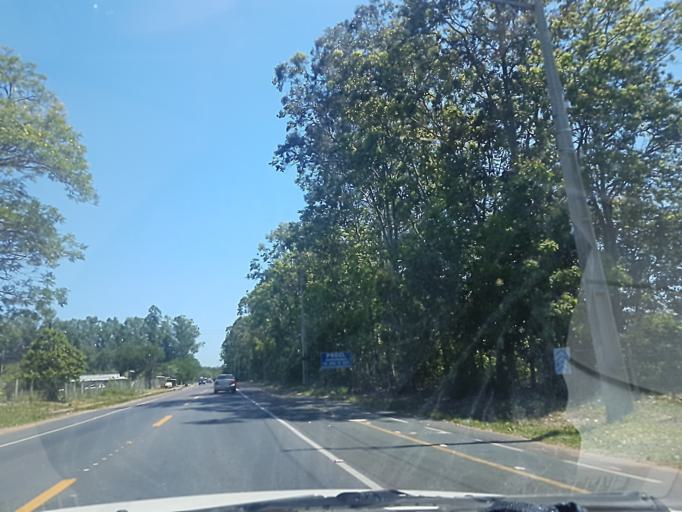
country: PY
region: Central
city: Limpio
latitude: -25.2220
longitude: -57.4179
